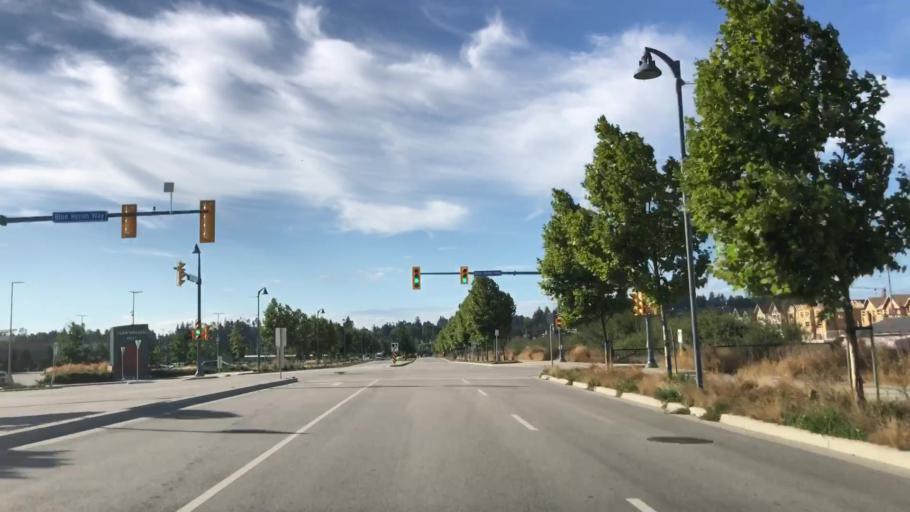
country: CA
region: British Columbia
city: Ladner
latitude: 49.0381
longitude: -123.0903
